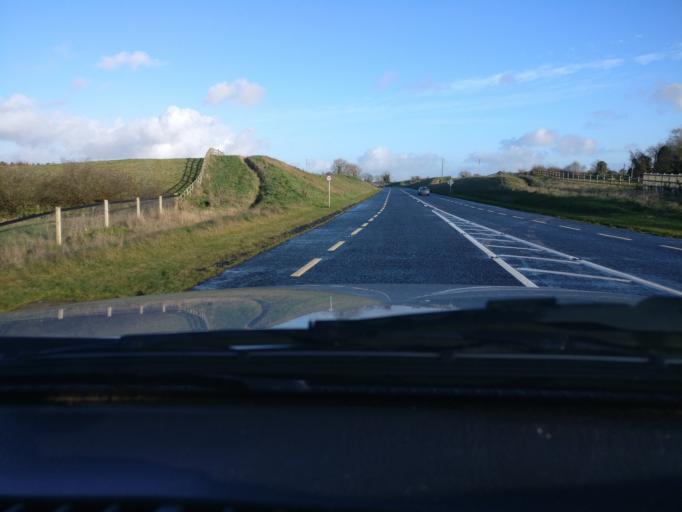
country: IE
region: Leinster
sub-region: An Iarmhi
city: Rathwire
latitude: 53.5573
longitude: -7.2242
